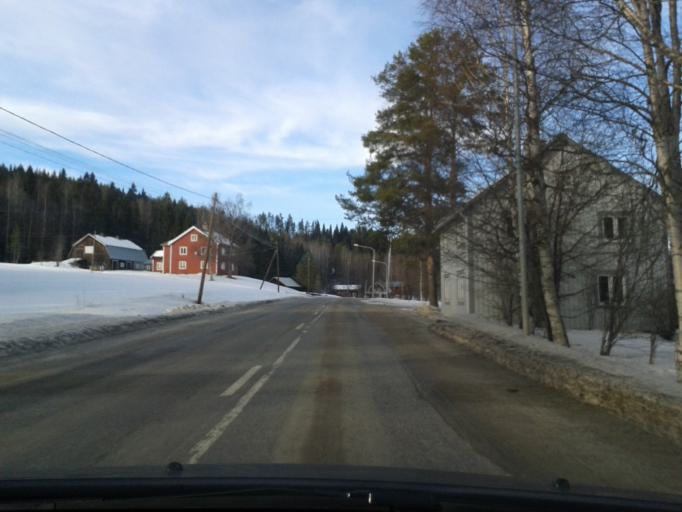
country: SE
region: Vaesternorrland
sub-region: OErnskoeldsviks Kommun
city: Bredbyn
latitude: 63.4908
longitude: 18.0814
